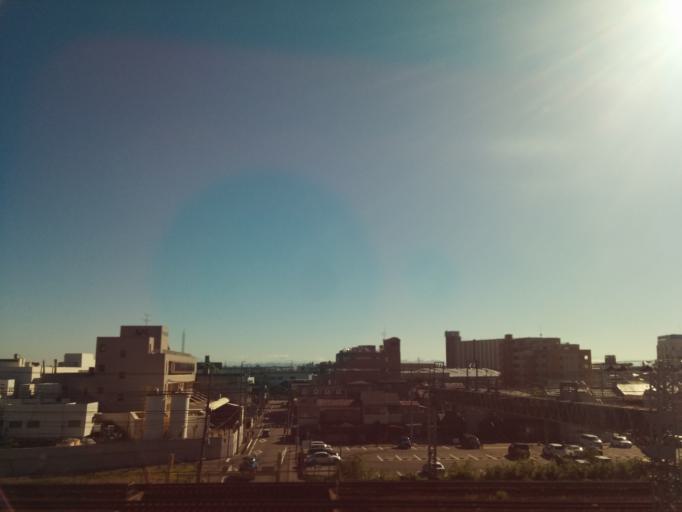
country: JP
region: Aichi
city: Nagoya-shi
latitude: 35.2008
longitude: 136.8592
